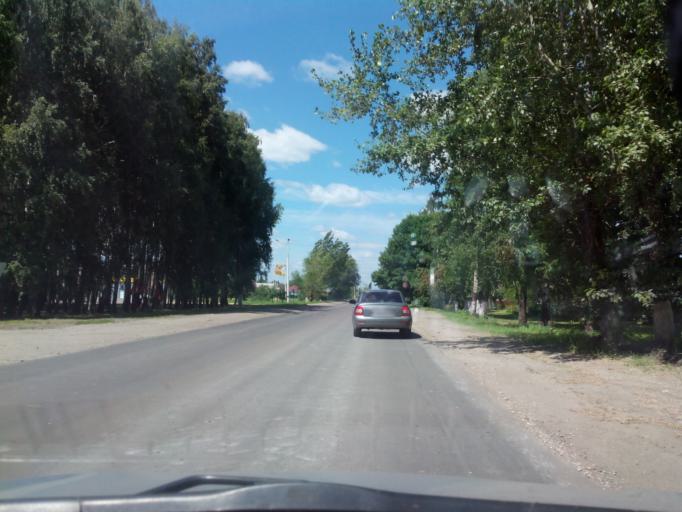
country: RU
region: Tambov
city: Zherdevka
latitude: 51.8213
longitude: 41.5040
